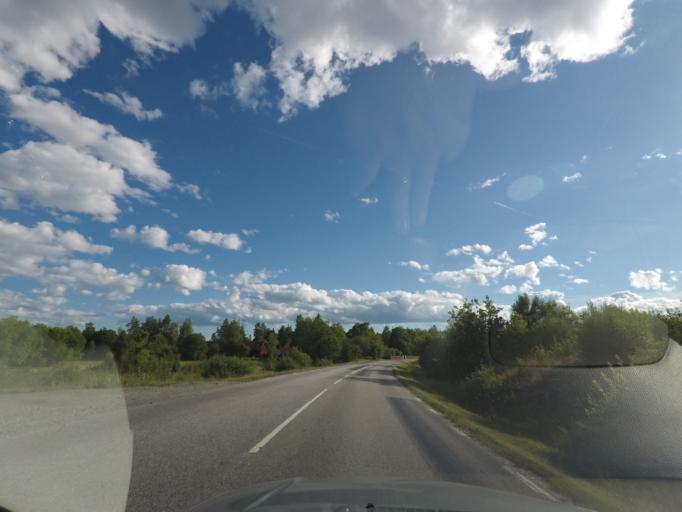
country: SE
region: Stockholm
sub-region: Sigtuna Kommun
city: Rosersberg
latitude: 59.6633
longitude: 17.9844
